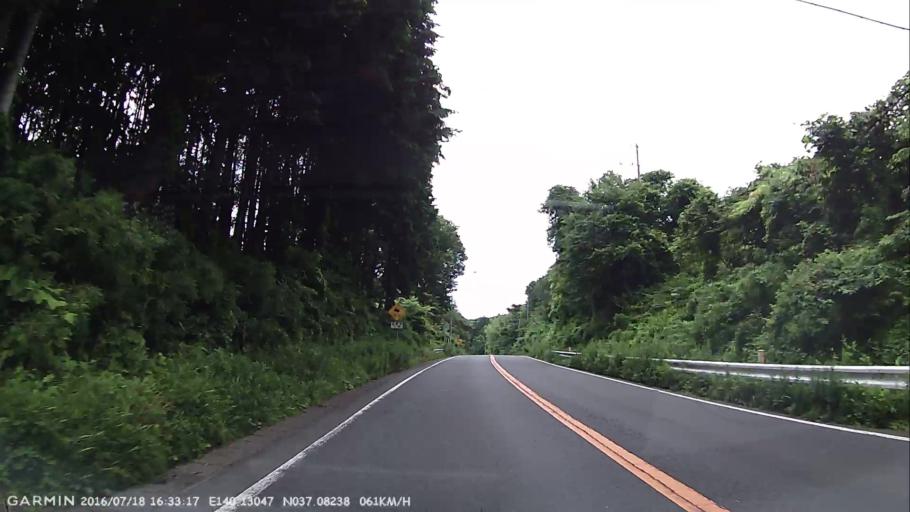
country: JP
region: Tochigi
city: Kuroiso
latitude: 37.0825
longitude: 140.1305
